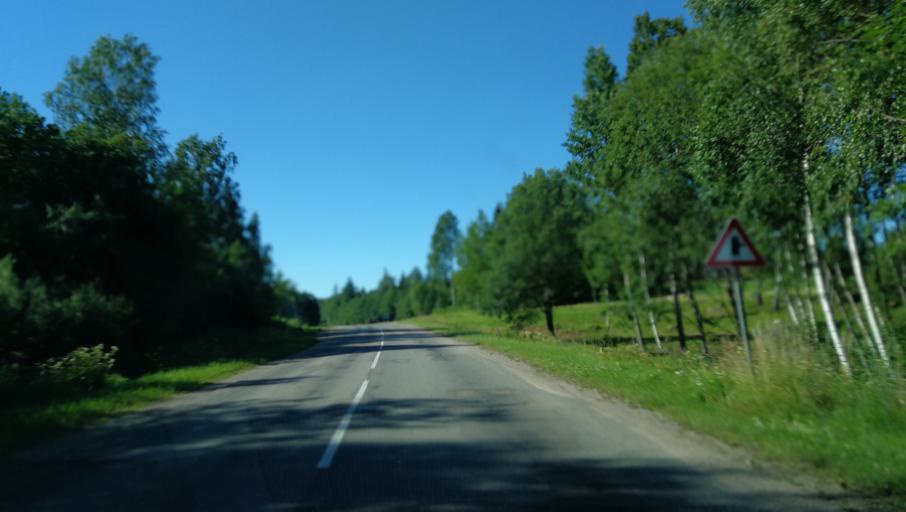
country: LV
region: Madonas Rajons
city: Madona
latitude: 56.9722
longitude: 26.0467
